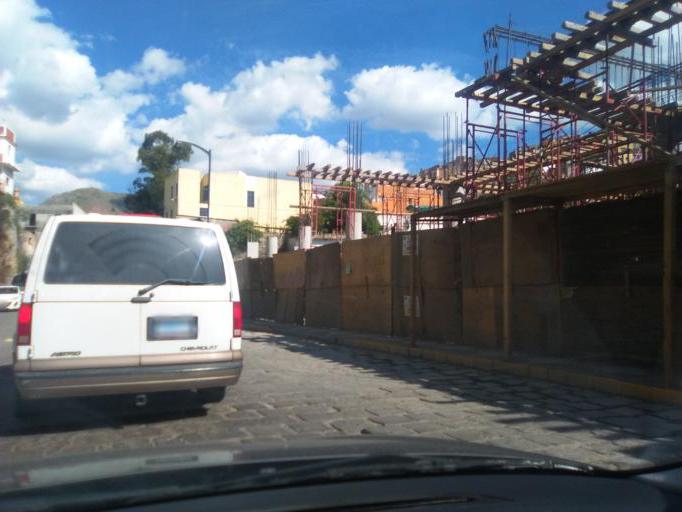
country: MX
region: Guanajuato
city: Guanajuato
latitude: 21.0185
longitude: -101.2627
